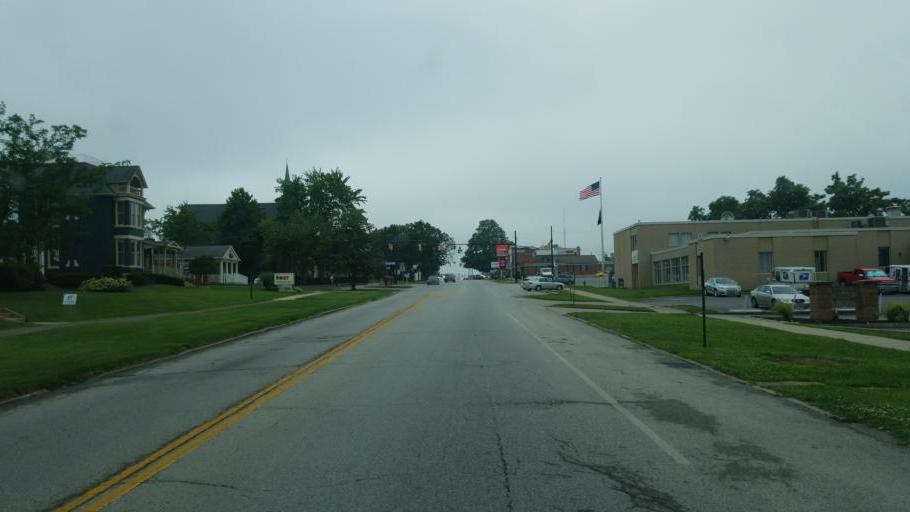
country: US
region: Ohio
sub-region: Highland County
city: Hillsboro
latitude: 39.2058
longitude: -83.6107
